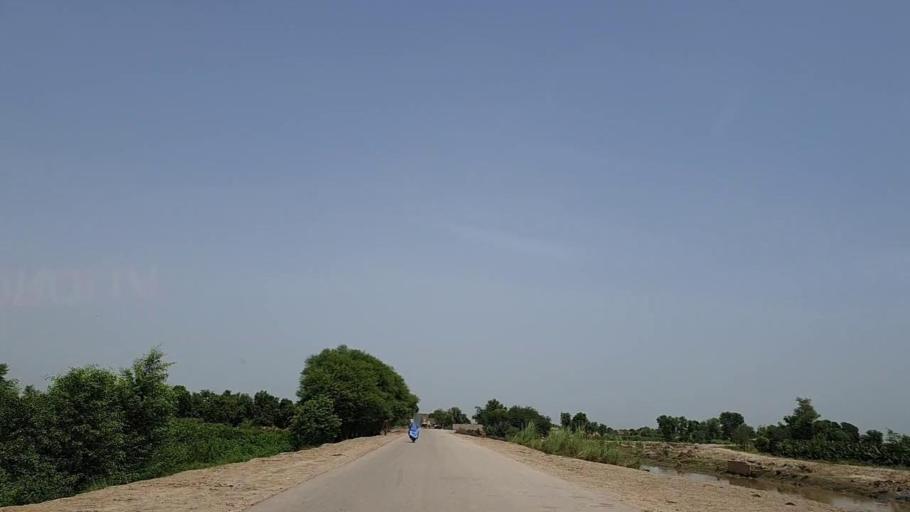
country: PK
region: Sindh
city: Tharu Shah
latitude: 26.8903
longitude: 68.0115
